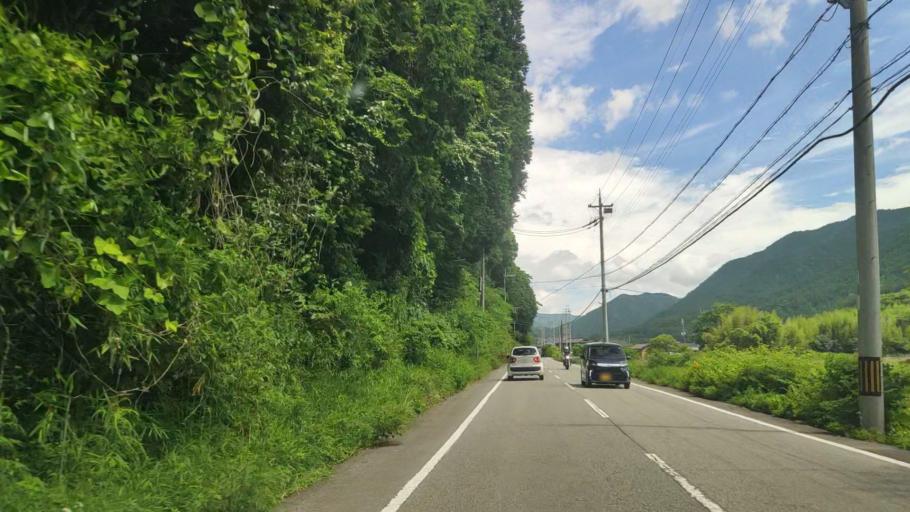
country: JP
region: Hyogo
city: Nishiwaki
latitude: 35.1614
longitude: 134.9284
